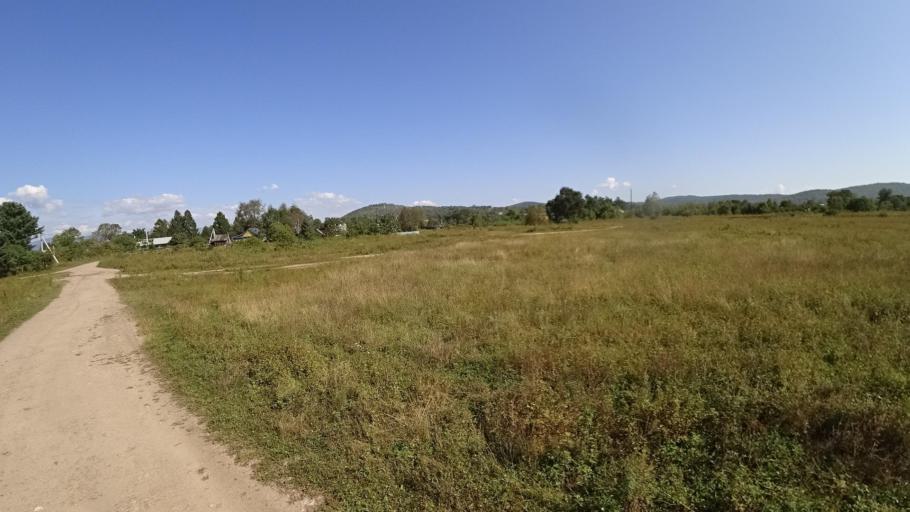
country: RU
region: Jewish Autonomous Oblast
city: Bira
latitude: 48.9941
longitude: 132.4544
